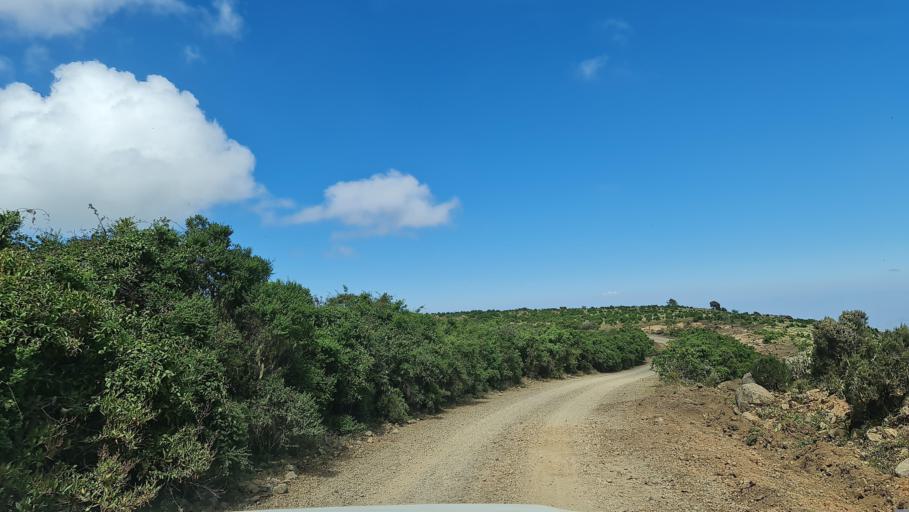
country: ET
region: Amhara
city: Debark'
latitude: 13.2317
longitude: 38.0231
